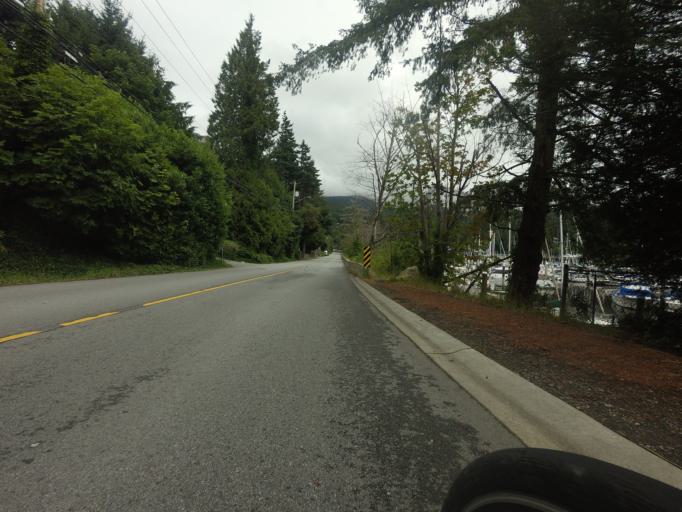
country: CA
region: British Columbia
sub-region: Greater Vancouver Regional District
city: Bowen Island
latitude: 49.3576
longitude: -123.2721
